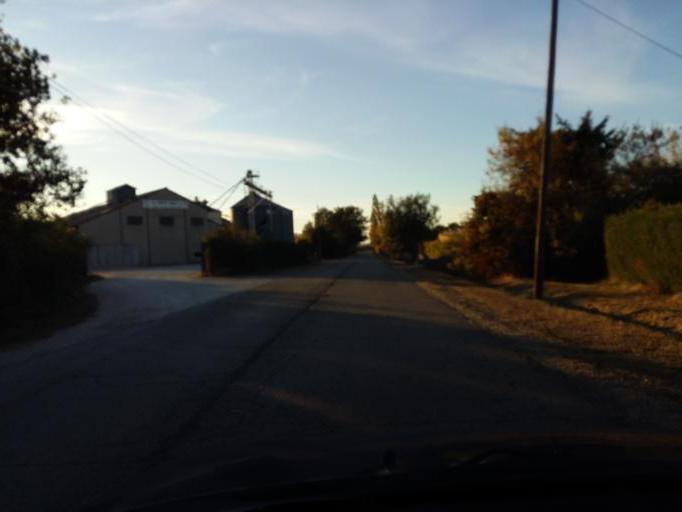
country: FR
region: Provence-Alpes-Cote d'Azur
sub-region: Departement du Vaucluse
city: Piolenc
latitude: 44.1836
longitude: 4.7456
